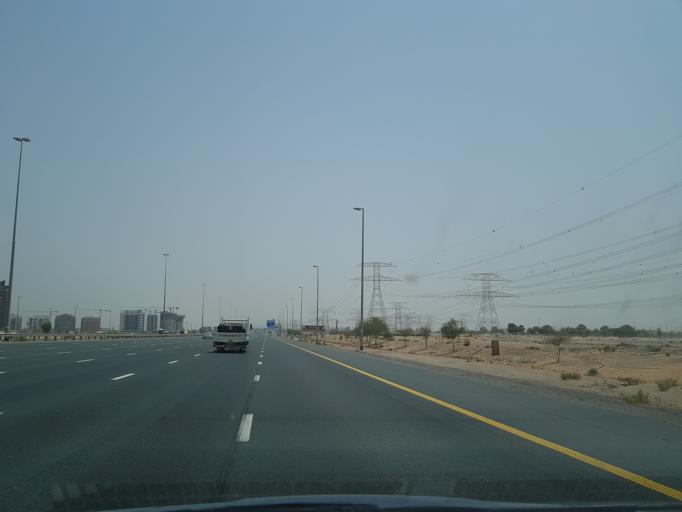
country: AE
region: Dubai
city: Dubai
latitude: 25.0790
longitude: 55.3806
